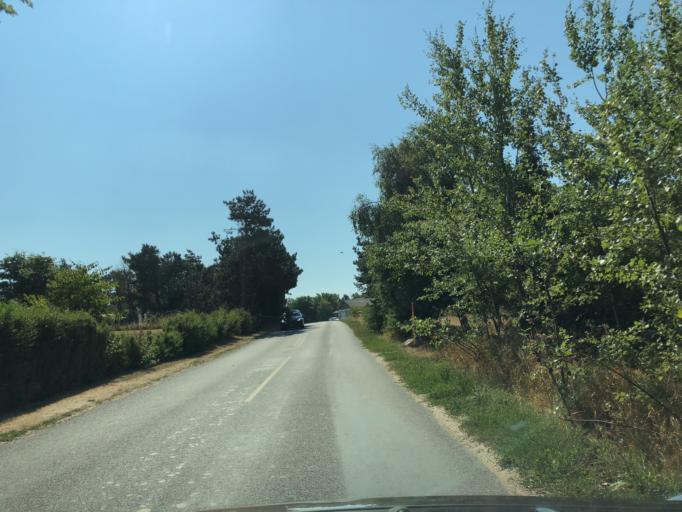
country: DK
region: Zealand
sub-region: Odsherred Kommune
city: Asnaes
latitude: 55.9852
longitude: 11.3021
